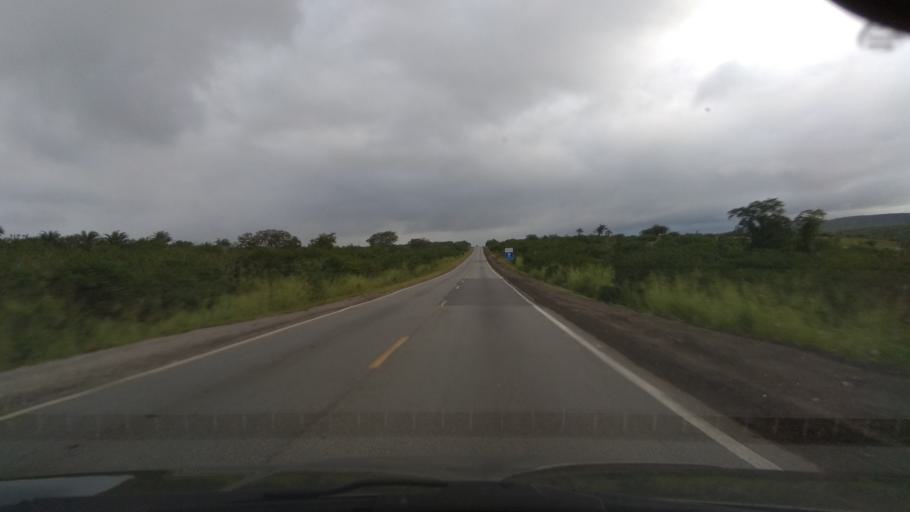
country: BR
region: Bahia
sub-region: Jaguaquara
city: Jaguaquara
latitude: -13.4147
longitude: -40.0262
